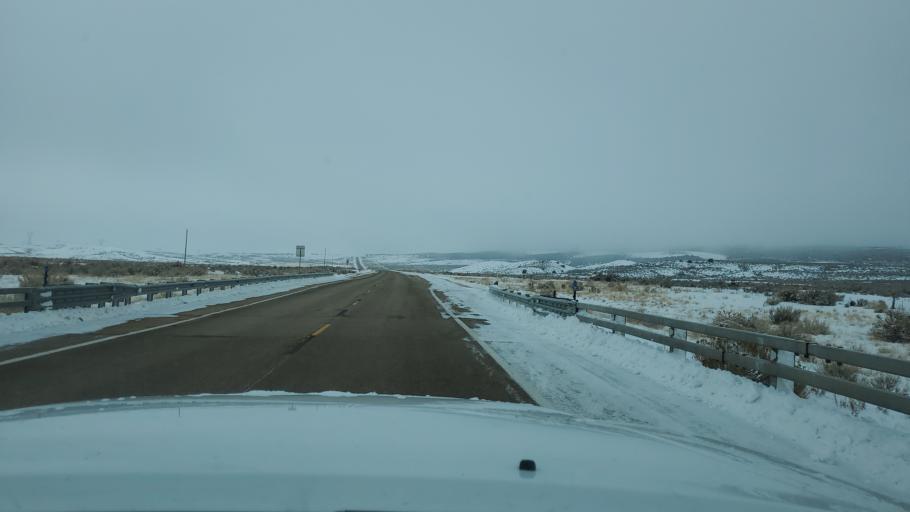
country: US
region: Colorado
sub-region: Rio Blanco County
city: Rangely
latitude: 40.2791
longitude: -108.5588
